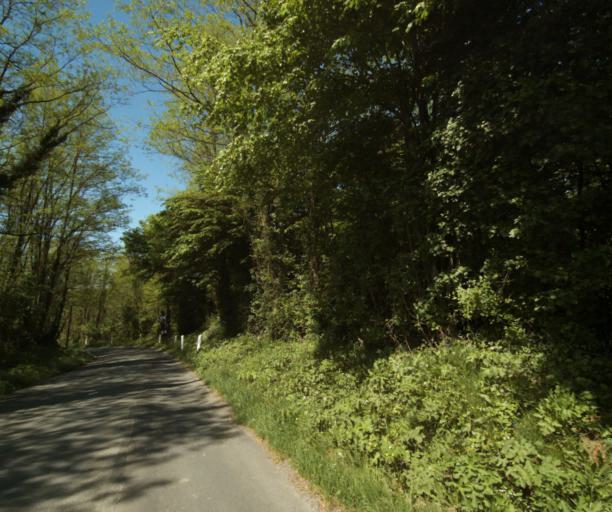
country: FR
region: Poitou-Charentes
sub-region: Departement de la Charente-Maritime
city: Ecoyeux
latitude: 45.7657
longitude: -0.4839
